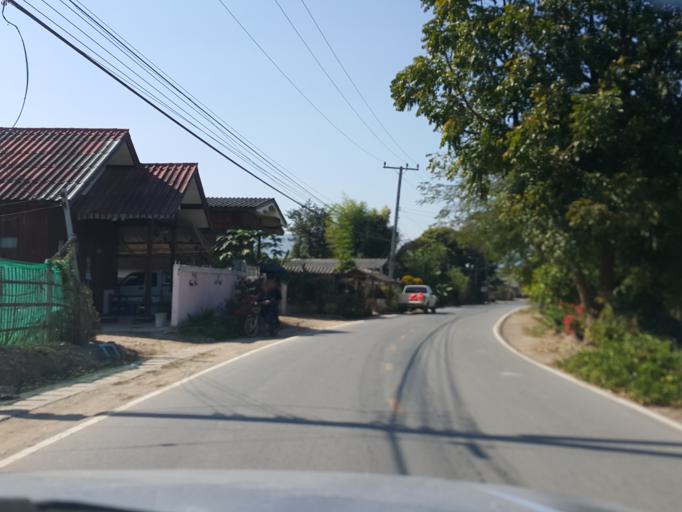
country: TH
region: Chiang Mai
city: Mae Wang
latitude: 18.5888
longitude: 98.7979
